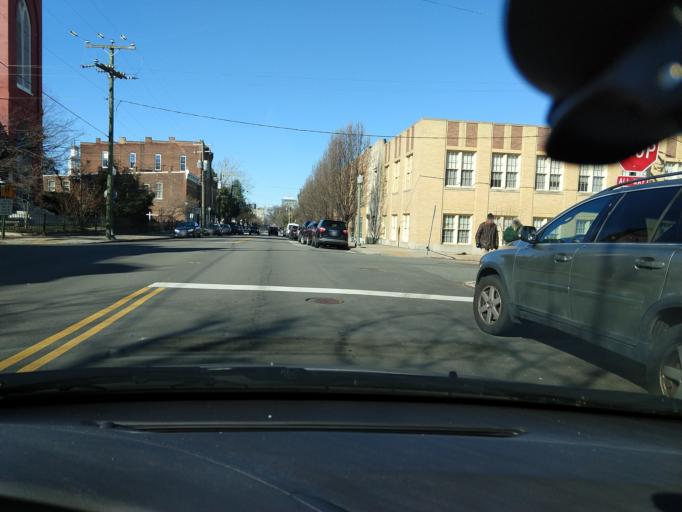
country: US
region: Virginia
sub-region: Henrico County
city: Montrose
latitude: 37.5307
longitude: -77.4175
